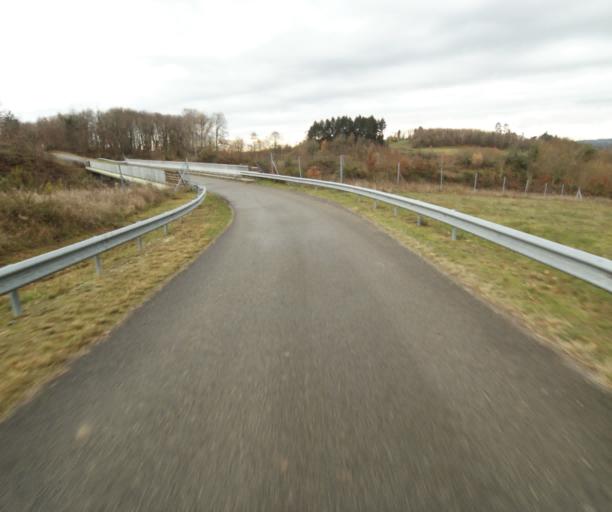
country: FR
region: Limousin
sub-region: Departement de la Correze
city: Saint-Mexant
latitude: 45.2910
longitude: 1.6330
